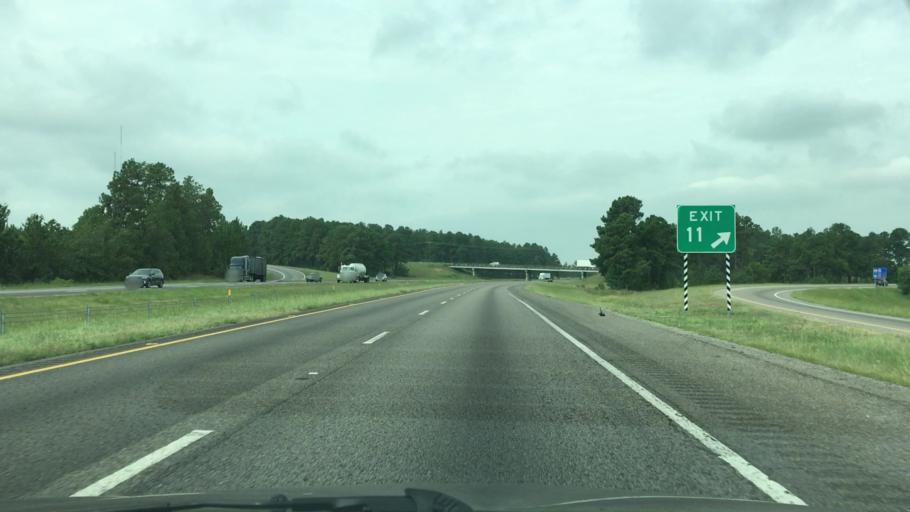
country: US
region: South Carolina
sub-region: Aiken County
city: Graniteville
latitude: 33.6088
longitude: -81.8401
